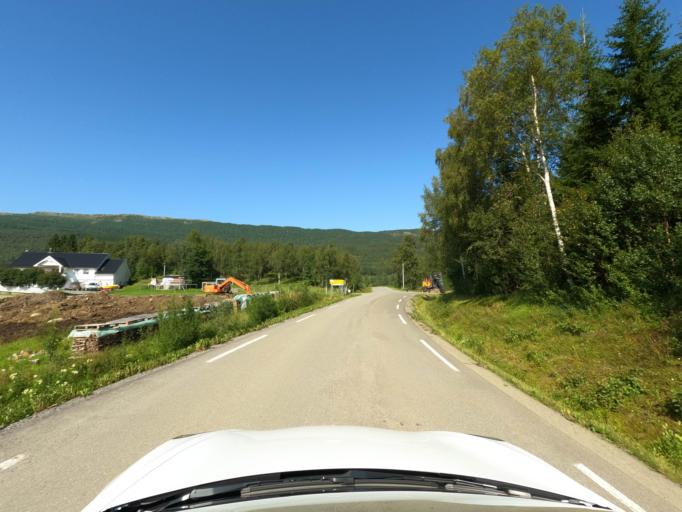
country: NO
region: Nordland
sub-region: Ballangen
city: Ballangen
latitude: 68.3463
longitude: 16.8050
